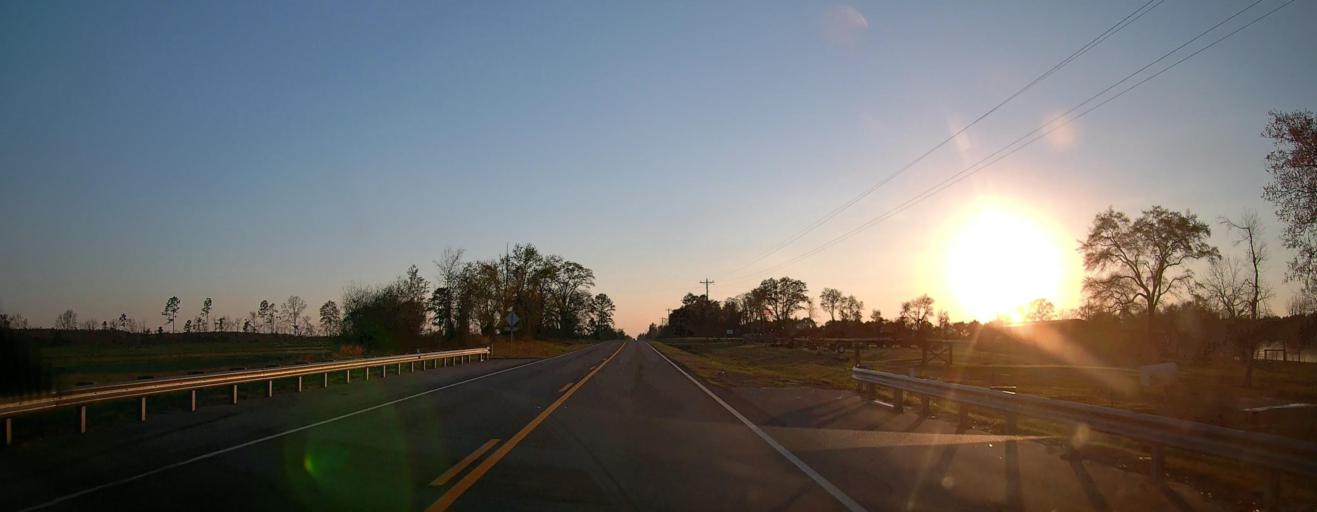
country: US
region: Georgia
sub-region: Dodge County
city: Chester
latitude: 32.3692
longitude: -83.0033
